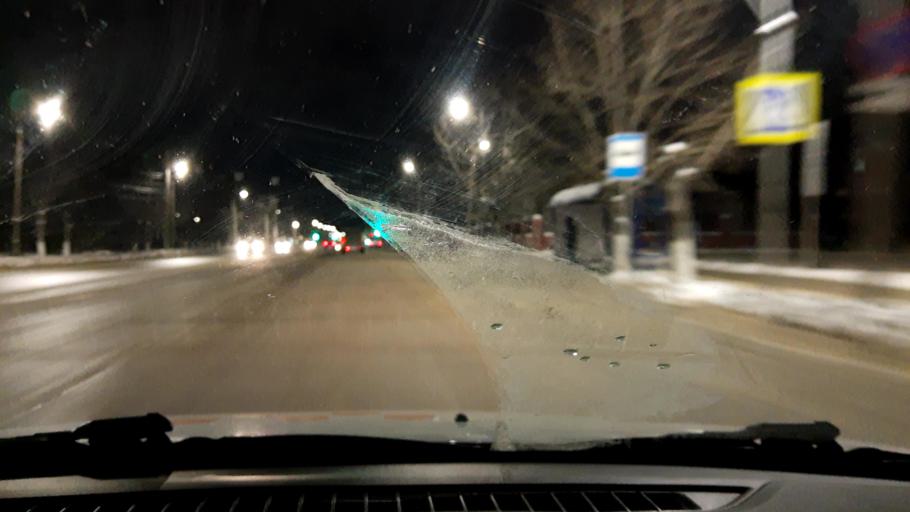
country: RU
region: Nizjnij Novgorod
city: Dzerzhinsk
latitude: 56.2376
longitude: 43.4865
